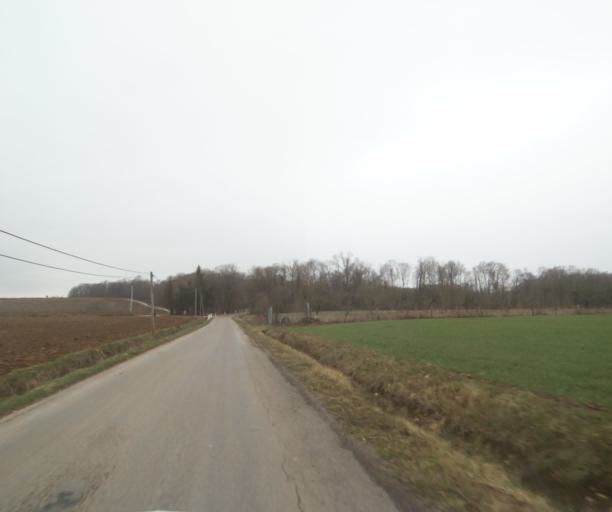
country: FR
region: Champagne-Ardenne
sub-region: Departement de la Haute-Marne
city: Wassy
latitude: 48.5382
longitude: 4.9822
